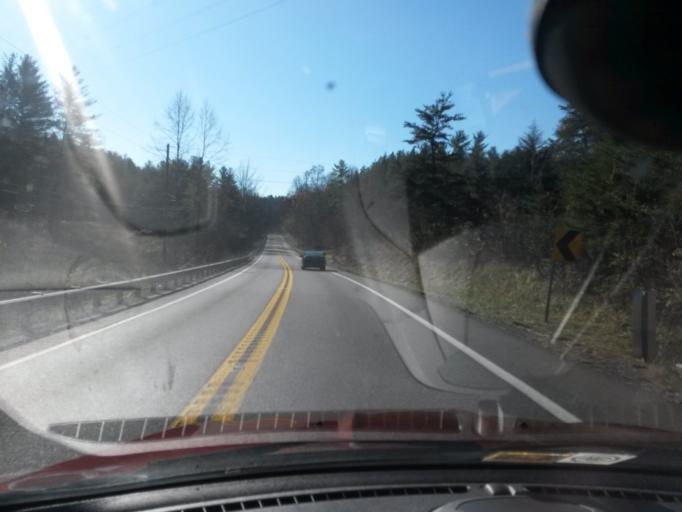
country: US
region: Virginia
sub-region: Alleghany County
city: Clifton Forge
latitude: 37.7059
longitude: -79.8154
